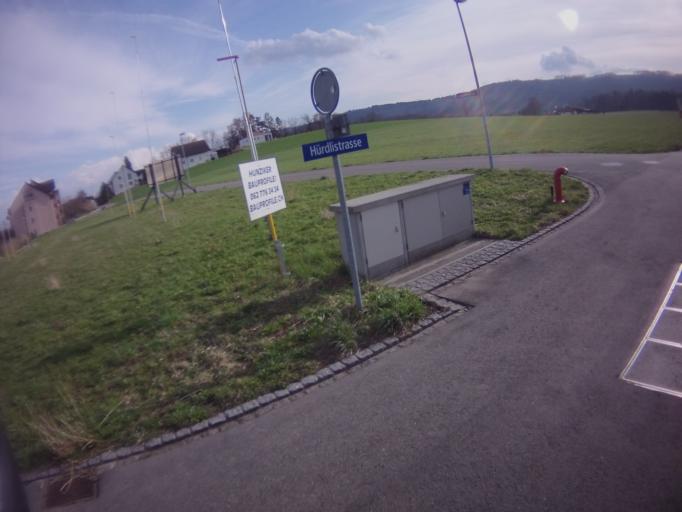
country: CH
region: Aargau
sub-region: Bezirk Baden
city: Wurenlos
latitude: 47.4437
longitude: 8.3584
